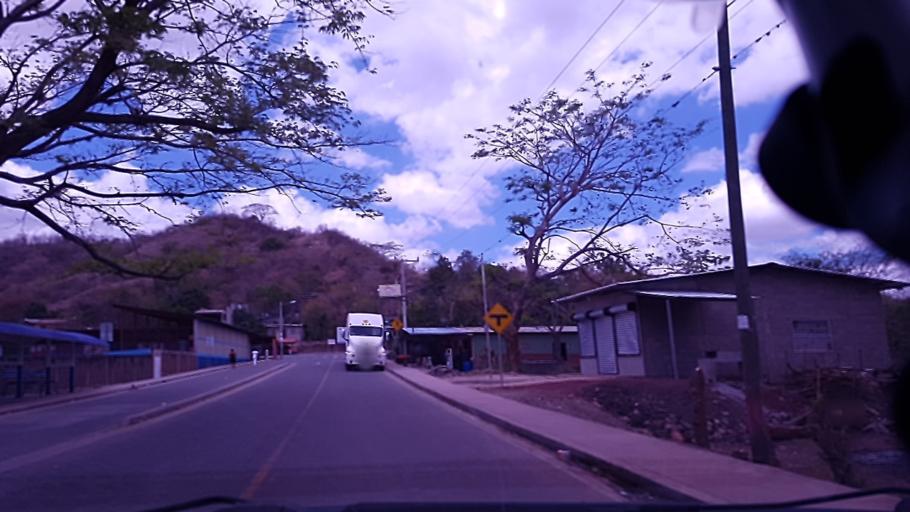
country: NI
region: Esteli
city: Condega
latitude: 13.3719
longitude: -86.3986
